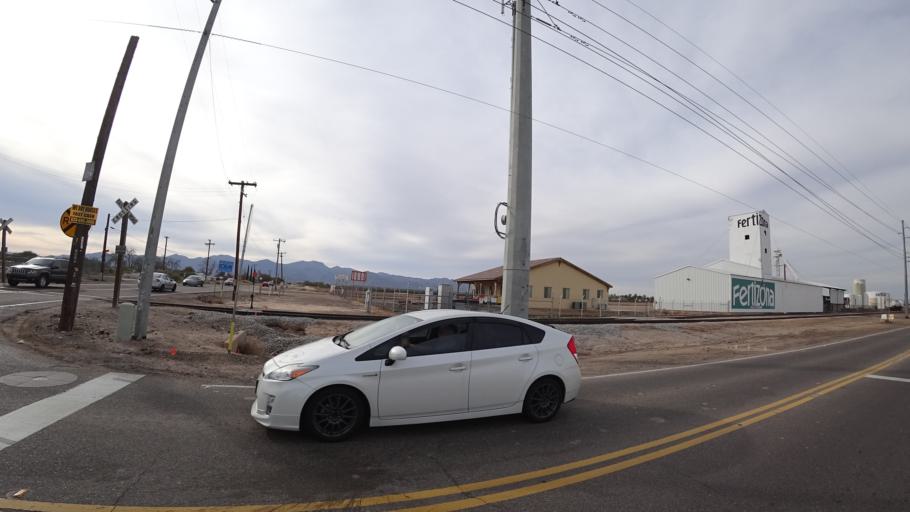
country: US
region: Arizona
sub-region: Maricopa County
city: Citrus Park
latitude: 33.5663
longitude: -112.4269
